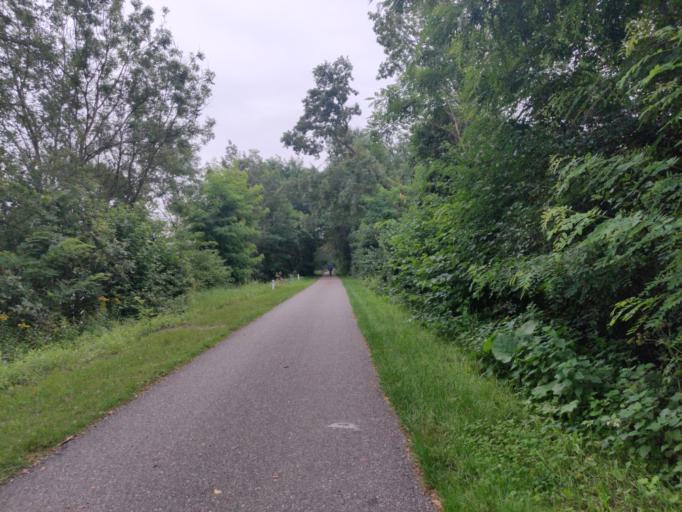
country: AT
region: Lower Austria
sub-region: Politischer Bezirk Tulln
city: Atzenbrugg
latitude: 48.3518
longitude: 15.8948
